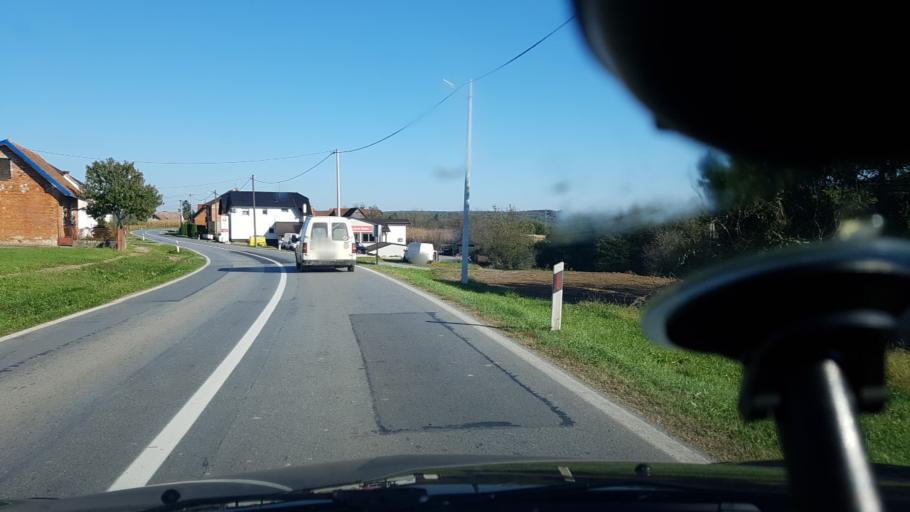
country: HR
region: Bjelovarsko-Bilogorska
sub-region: Grad Cazma
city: Cazma
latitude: 45.7813
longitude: 16.6680
